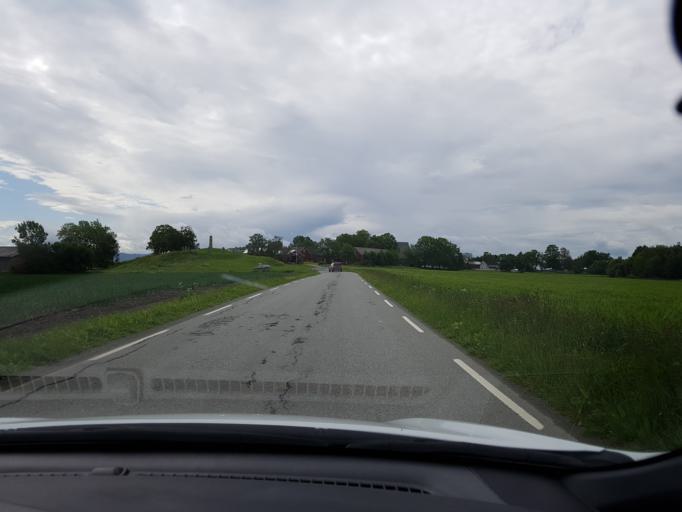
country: NO
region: Nord-Trondelag
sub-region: Frosta
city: Frosta
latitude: 63.5699
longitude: 10.7043
